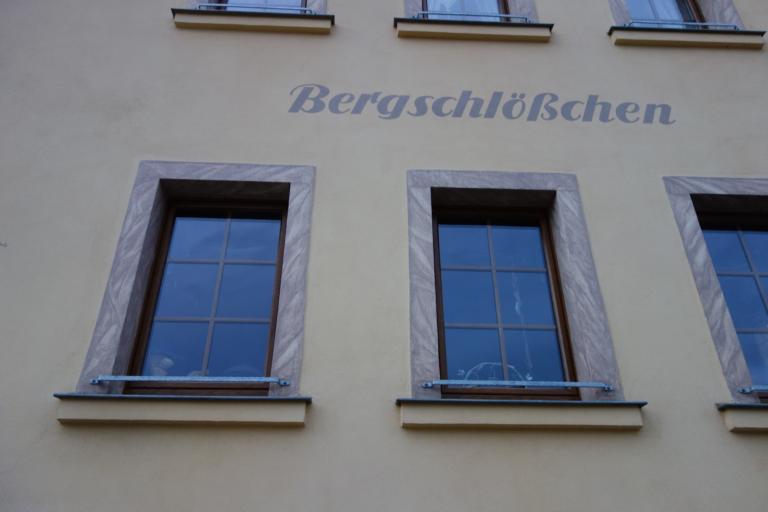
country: DE
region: Saxony
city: Pockau
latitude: 50.7006
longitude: 13.2290
